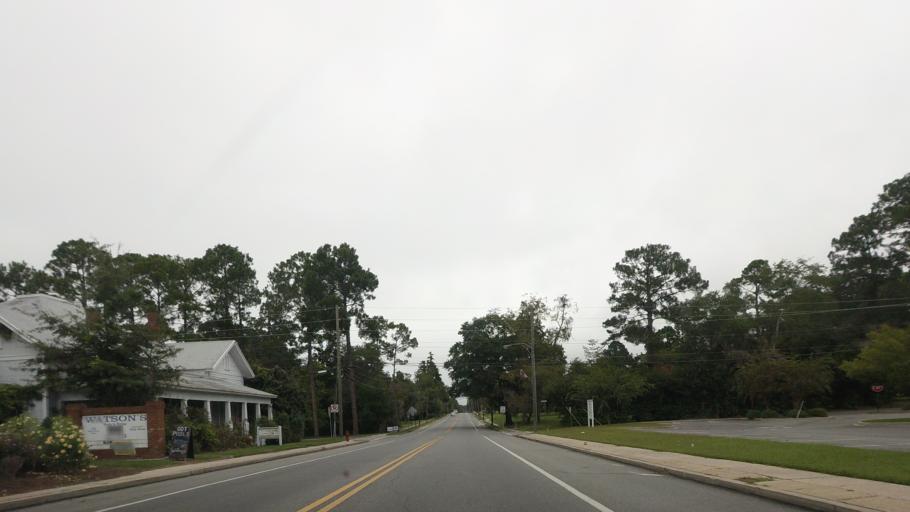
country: US
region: Georgia
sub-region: Berrien County
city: Nashville
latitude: 31.2090
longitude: -83.2500
